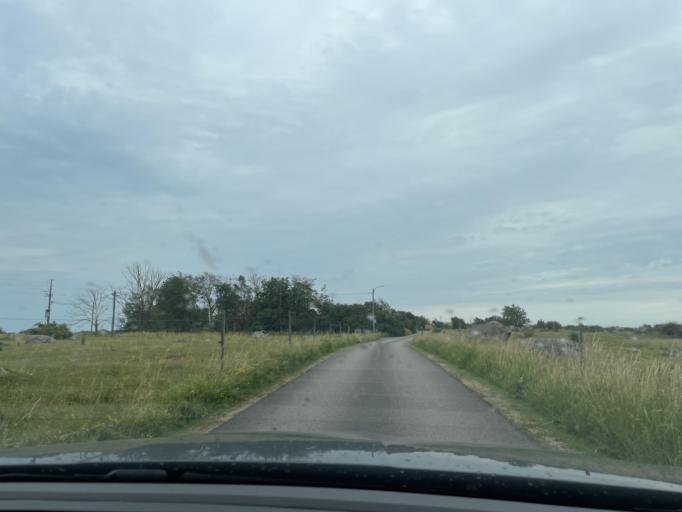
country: SE
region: Skane
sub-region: Bromolla Kommun
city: Bromoella
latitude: 56.0009
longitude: 14.4433
